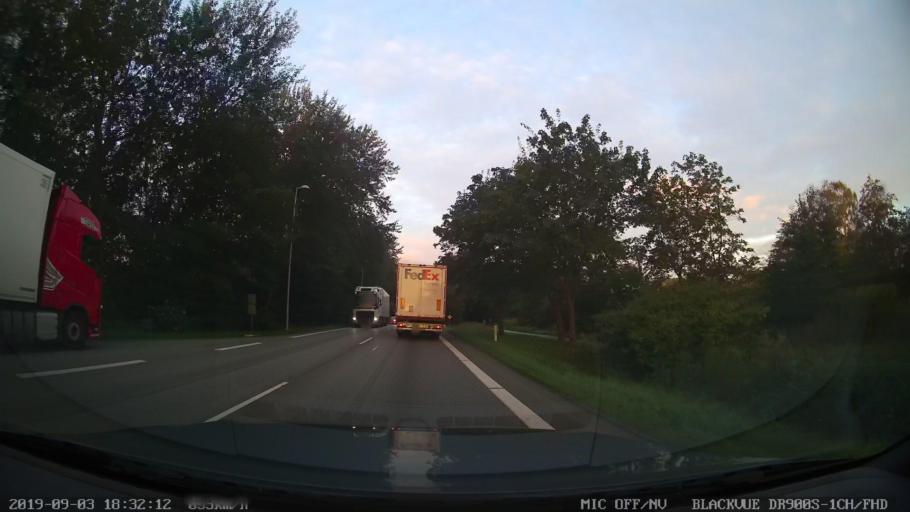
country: DK
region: Capital Region
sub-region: Helsingor Kommune
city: Espergaerde
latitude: 56.0177
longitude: 12.5591
